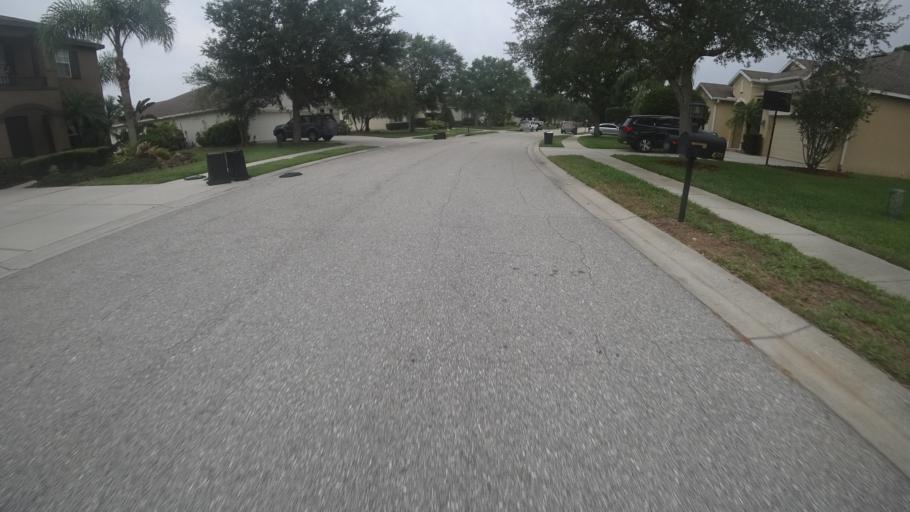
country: US
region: Florida
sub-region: Manatee County
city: Samoset
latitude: 27.4339
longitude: -82.5115
